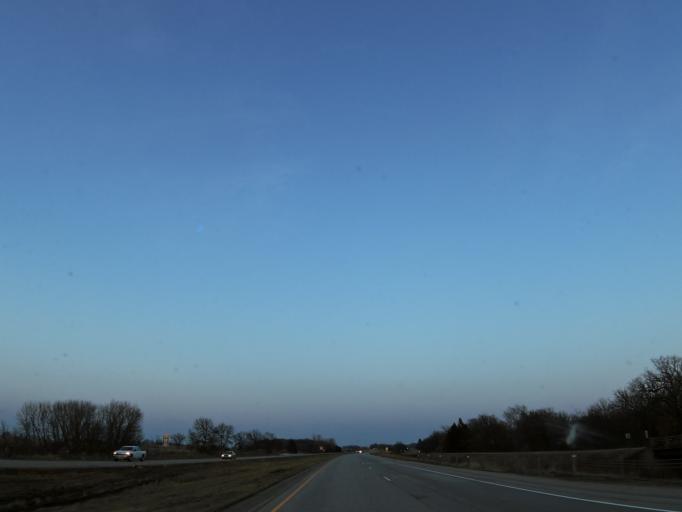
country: US
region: Minnesota
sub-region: Mower County
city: Grand Meadow
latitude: 43.6743
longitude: -92.7642
